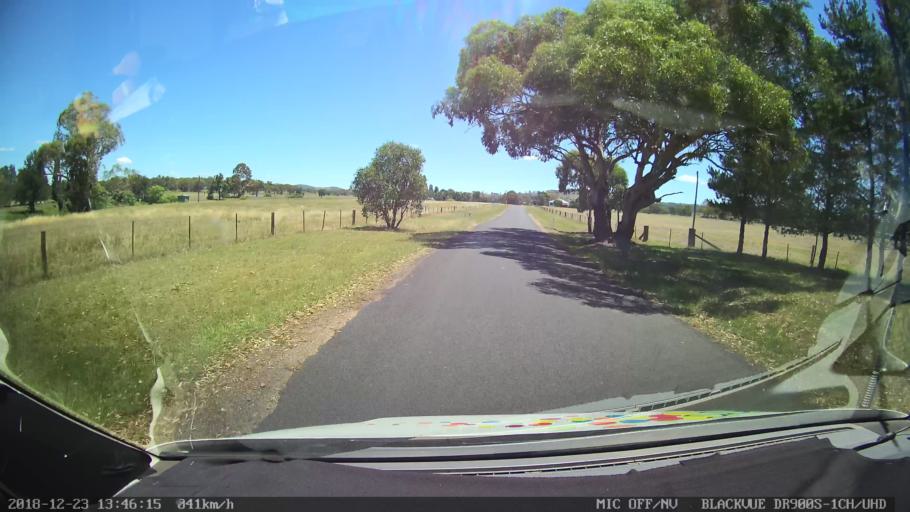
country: AU
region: New South Wales
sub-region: Tamworth Municipality
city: Manilla
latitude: -30.5047
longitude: 151.1204
